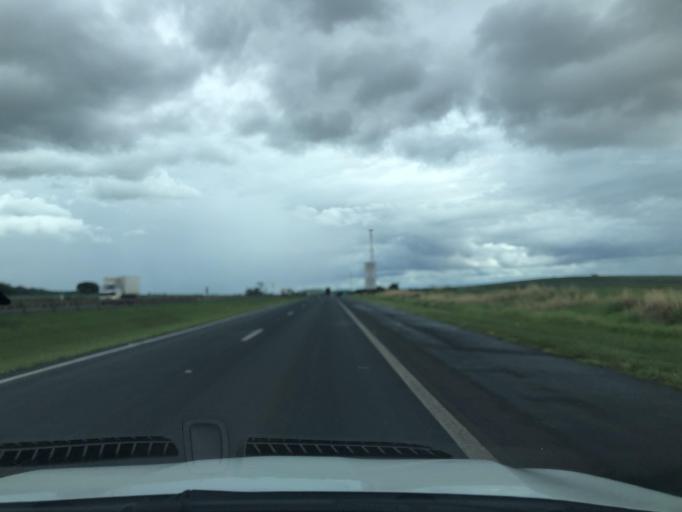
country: BR
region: Sao Paulo
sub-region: Igarapava
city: Igarapava
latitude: -20.1770
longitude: -47.7872
